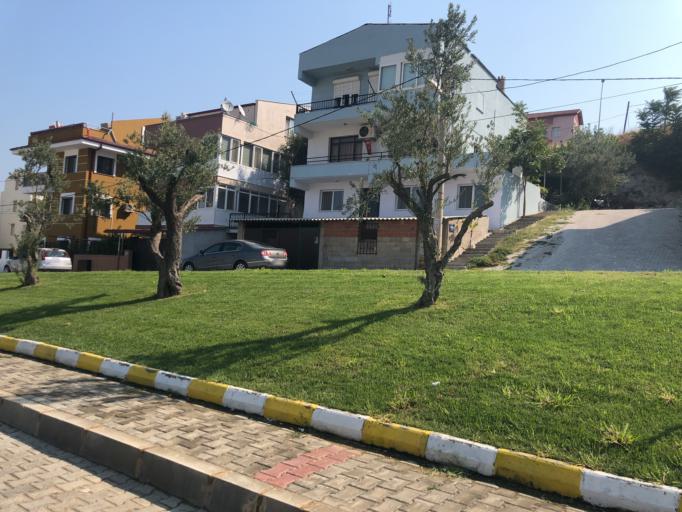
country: TR
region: Izmir
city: Urla
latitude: 38.3262
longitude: 26.7643
